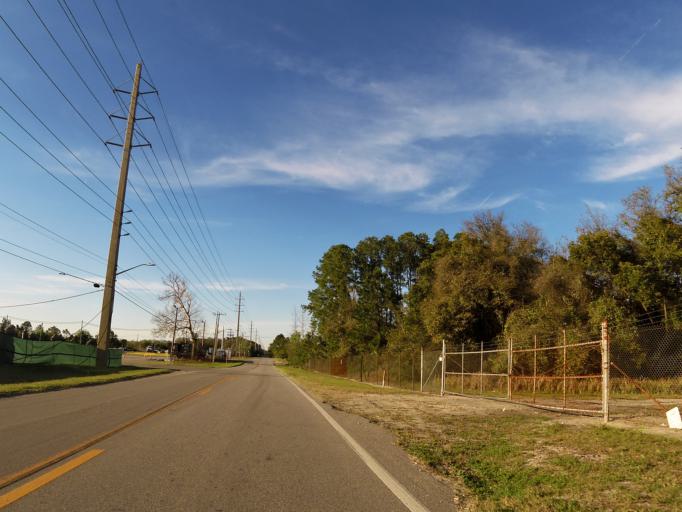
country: US
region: Florida
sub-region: Duval County
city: Jacksonville
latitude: 30.4229
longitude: -81.6013
